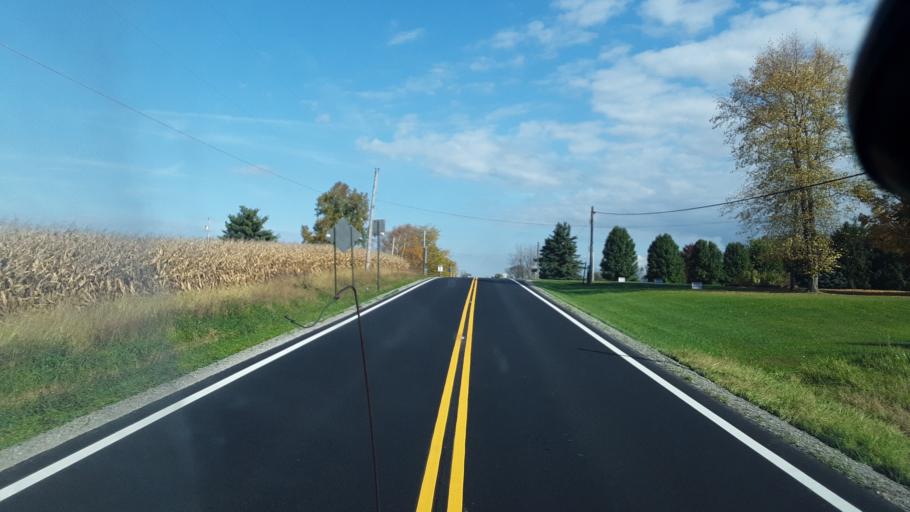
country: US
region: Ohio
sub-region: Highland County
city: Leesburg
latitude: 39.2971
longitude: -83.5902
